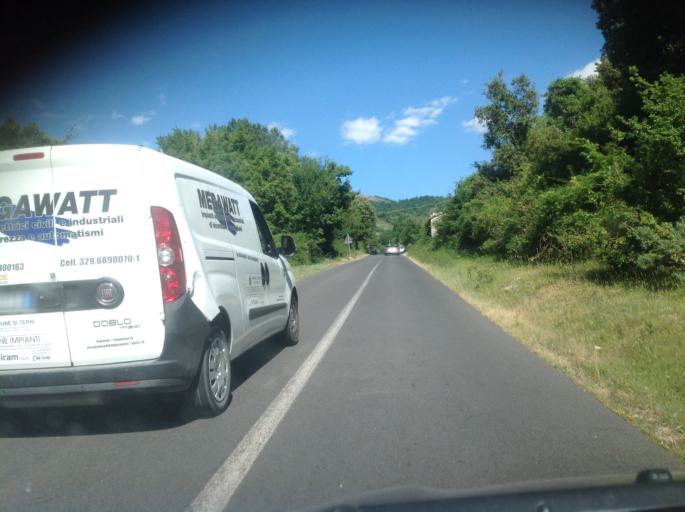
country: IT
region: Umbria
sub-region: Provincia di Terni
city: Stroncone
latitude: 42.4777
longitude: 12.6686
